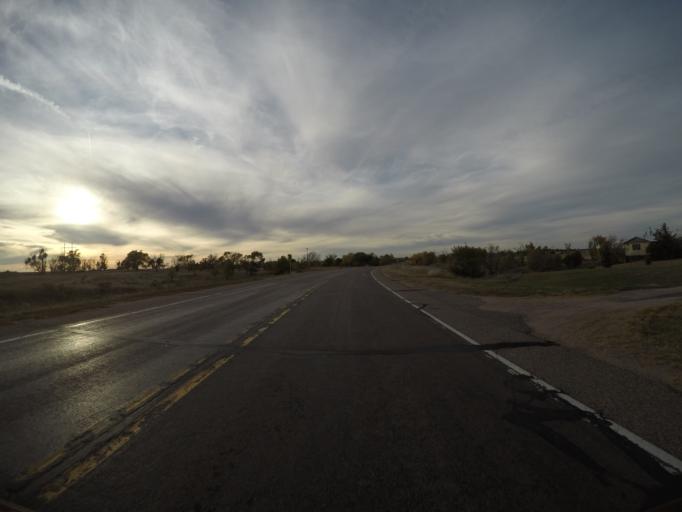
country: US
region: Colorado
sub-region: Yuma County
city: Yuma
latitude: 39.6557
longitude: -102.8430
